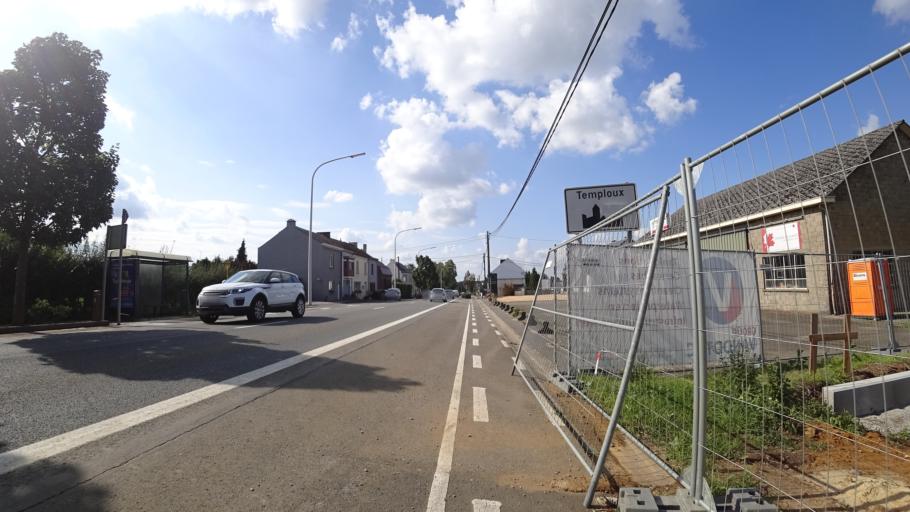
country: BE
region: Wallonia
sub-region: Province de Namur
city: Floreffe
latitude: 50.4810
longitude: 4.7690
